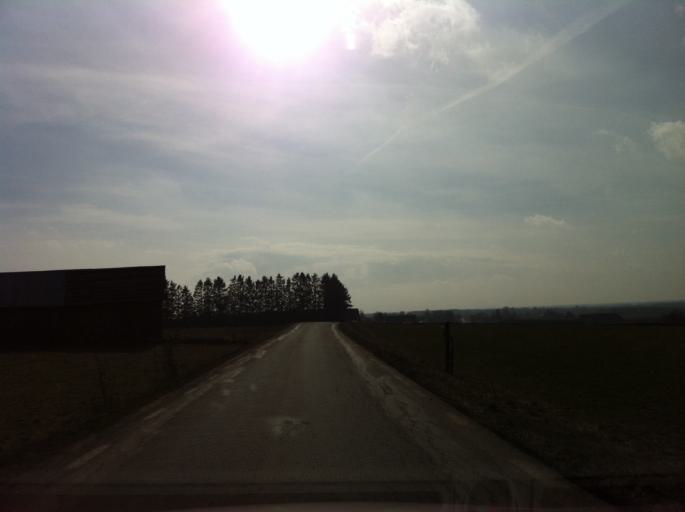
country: SE
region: Vaestra Goetaland
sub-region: Falkopings Kommun
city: Falkoeping
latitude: 58.2162
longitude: 13.4654
